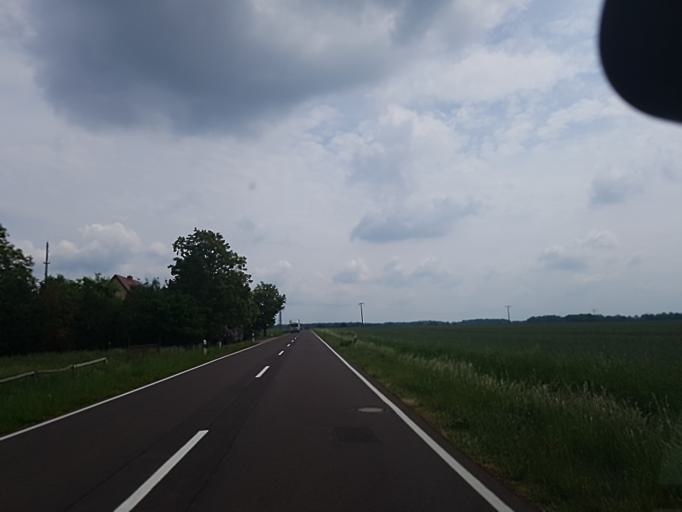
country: DE
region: Saxony-Anhalt
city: Loburg
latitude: 52.1126
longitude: 12.0979
